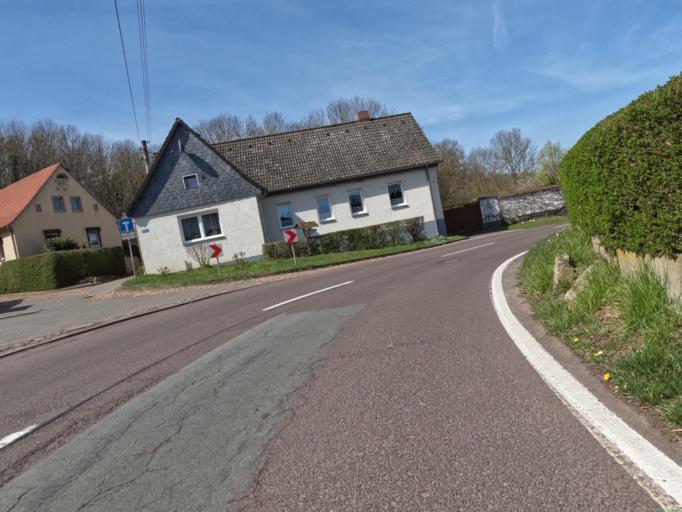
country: DE
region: Saxony-Anhalt
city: Beesenstedt
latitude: 51.5796
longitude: 11.7656
